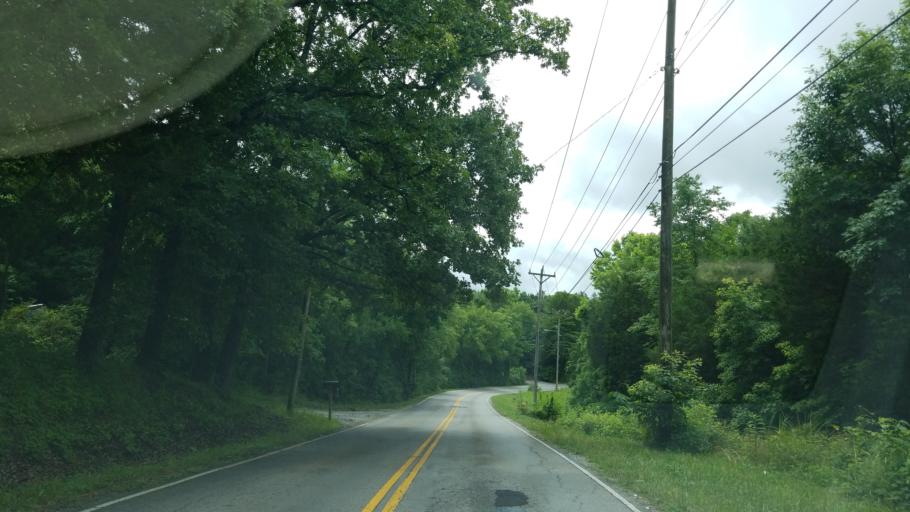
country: US
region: Tennessee
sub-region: Rutherford County
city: La Vergne
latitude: 36.0557
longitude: -86.6680
